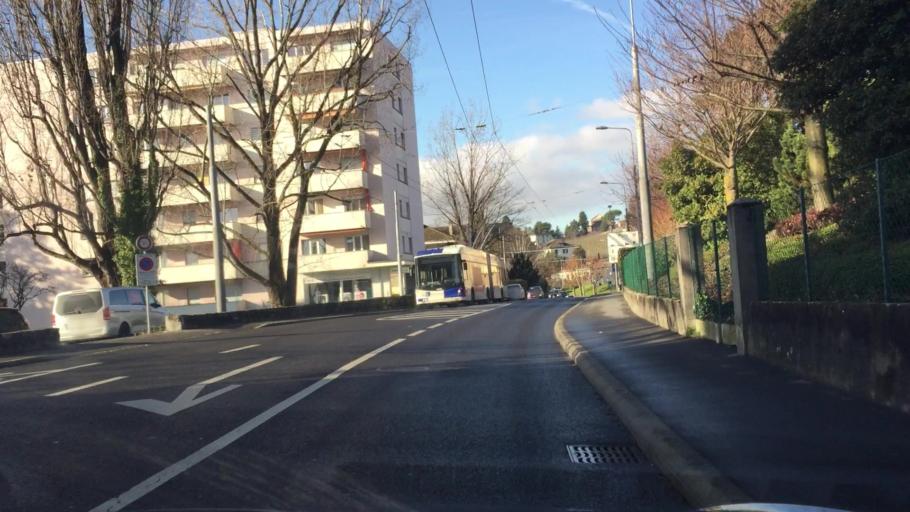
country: CH
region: Vaud
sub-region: Lavaux-Oron District
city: Paudex
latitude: 46.5066
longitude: 6.6682
